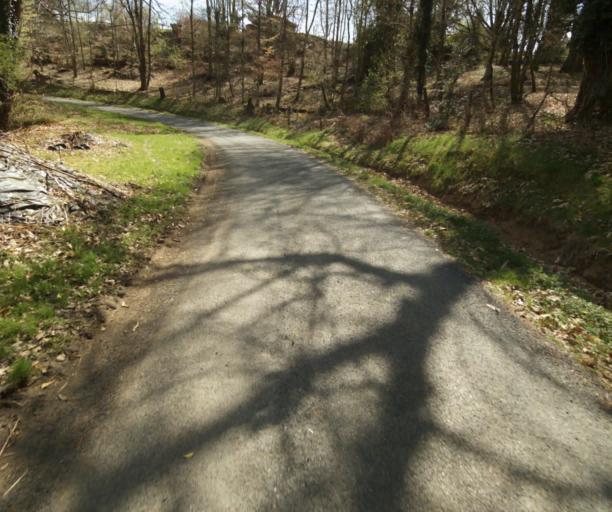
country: FR
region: Limousin
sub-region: Departement de la Correze
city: Seilhac
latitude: 45.3952
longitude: 1.7674
